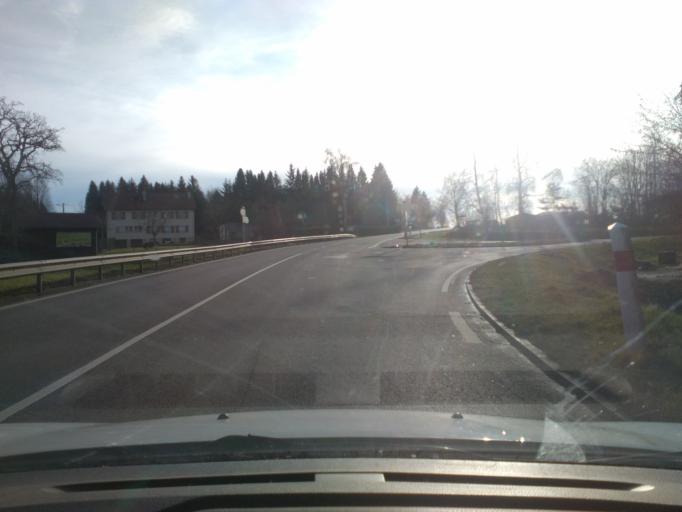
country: FR
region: Lorraine
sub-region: Departement des Vosges
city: Anould
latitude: 48.1666
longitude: 6.9191
